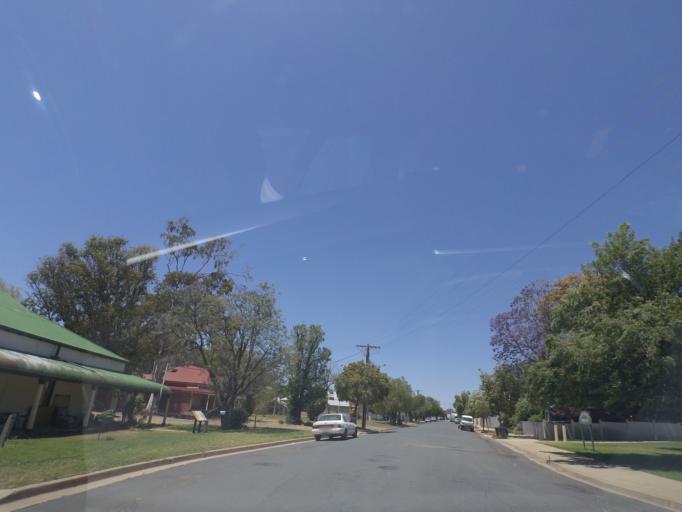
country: AU
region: New South Wales
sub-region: Berrigan
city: Berrigan
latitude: -35.3549
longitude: 145.7259
